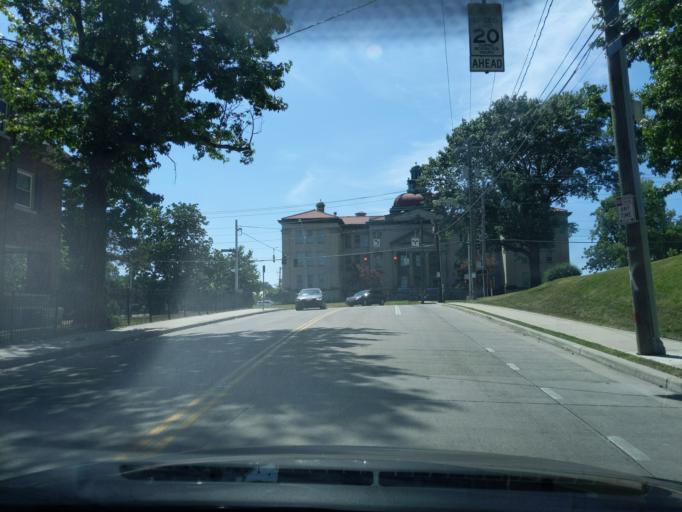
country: US
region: Ohio
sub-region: Hamilton County
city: Saint Bernard
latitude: 39.1502
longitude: -84.5178
